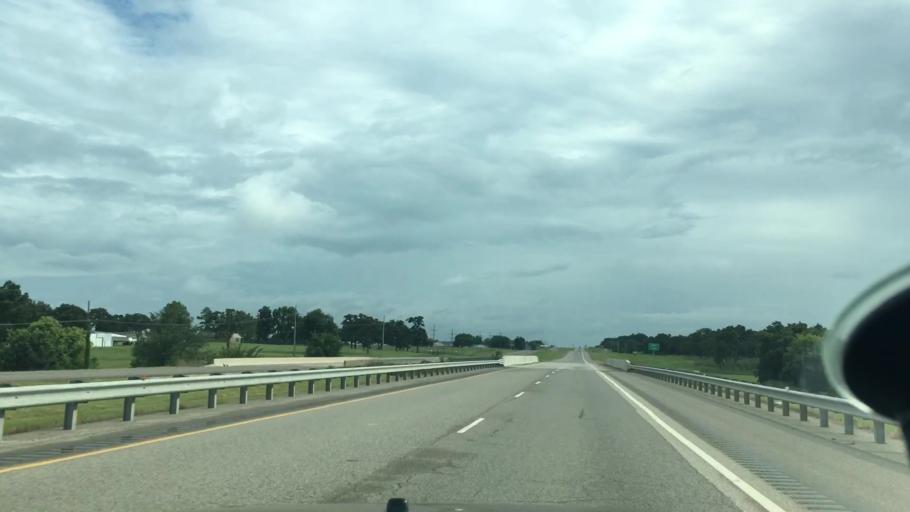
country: US
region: Oklahoma
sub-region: Lincoln County
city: Prague
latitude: 35.3614
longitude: -96.6718
